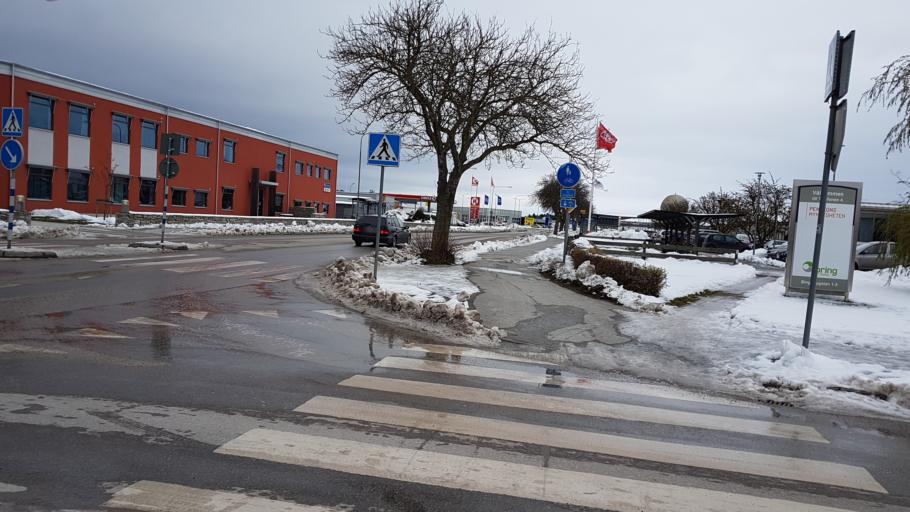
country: SE
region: Gotland
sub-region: Gotland
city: Visby
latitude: 57.6438
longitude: 18.3137
